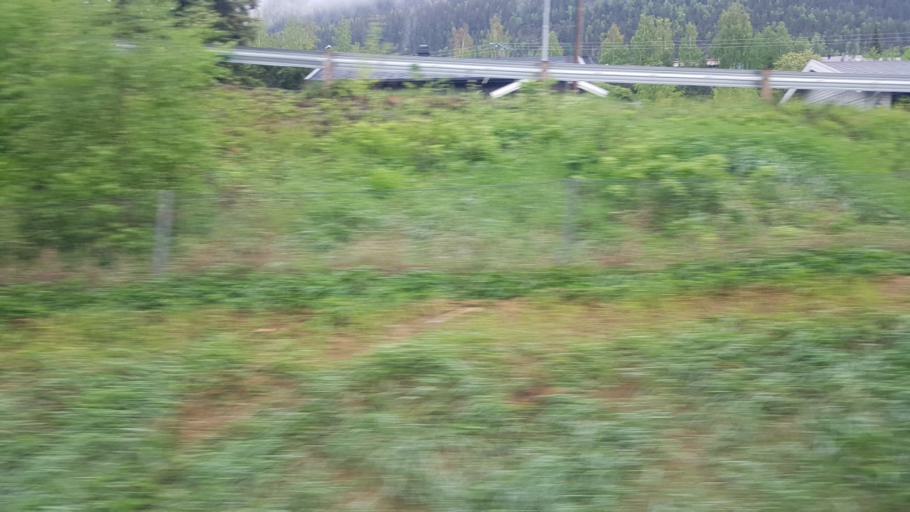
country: NO
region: Oppland
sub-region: Sor-Fron
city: Hundorp
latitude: 61.5698
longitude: 9.8647
